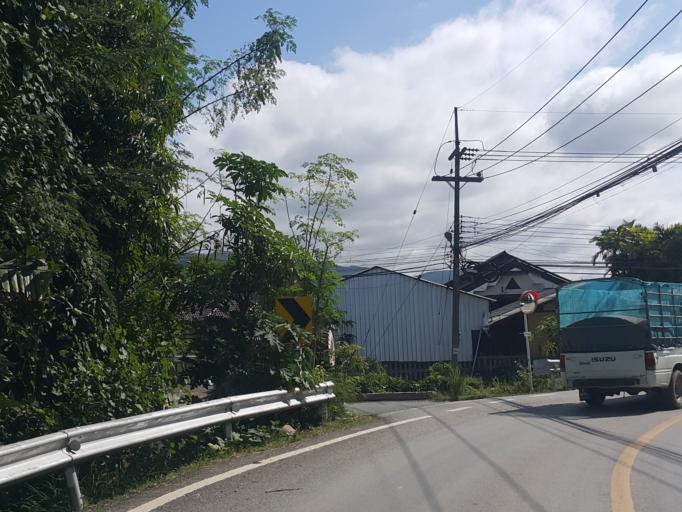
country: TH
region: Chiang Mai
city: San Kamphaeng
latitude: 18.6914
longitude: 99.1585
